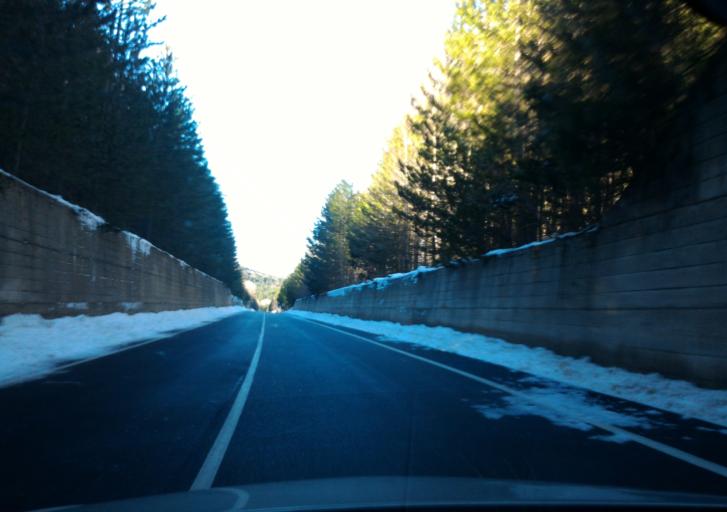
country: IT
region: Calabria
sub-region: Provincia di Cosenza
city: Celico
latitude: 39.3344
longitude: 16.4754
